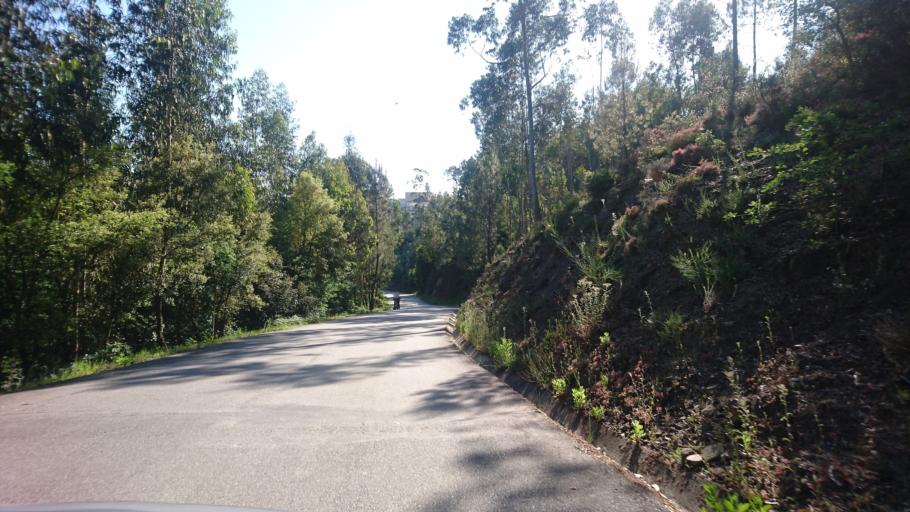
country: PT
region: Porto
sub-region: Paredes
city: Recarei
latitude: 41.1518
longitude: -8.3857
